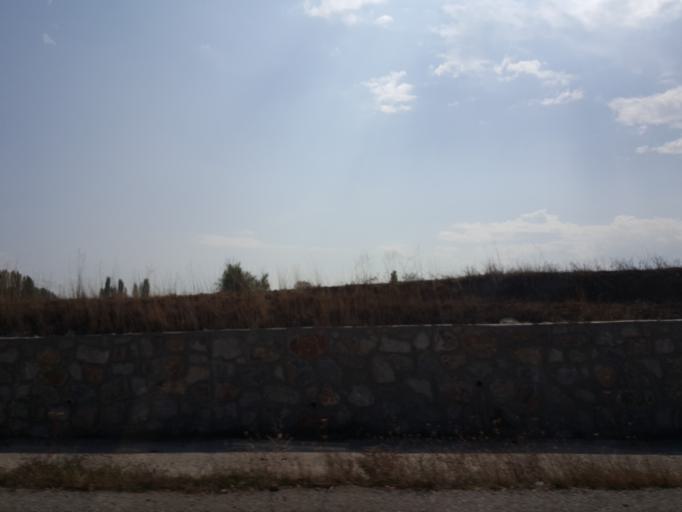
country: TR
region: Corum
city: Alaca
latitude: 40.1483
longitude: 34.8421
